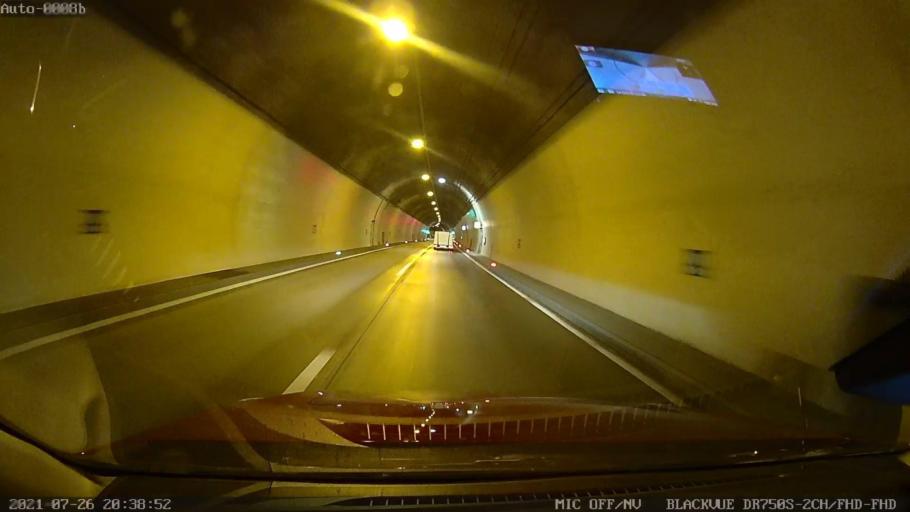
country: AT
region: Styria
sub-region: Politischer Bezirk Graz-Umgebung
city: Deutschfeistritz
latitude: 47.1985
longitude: 15.3249
